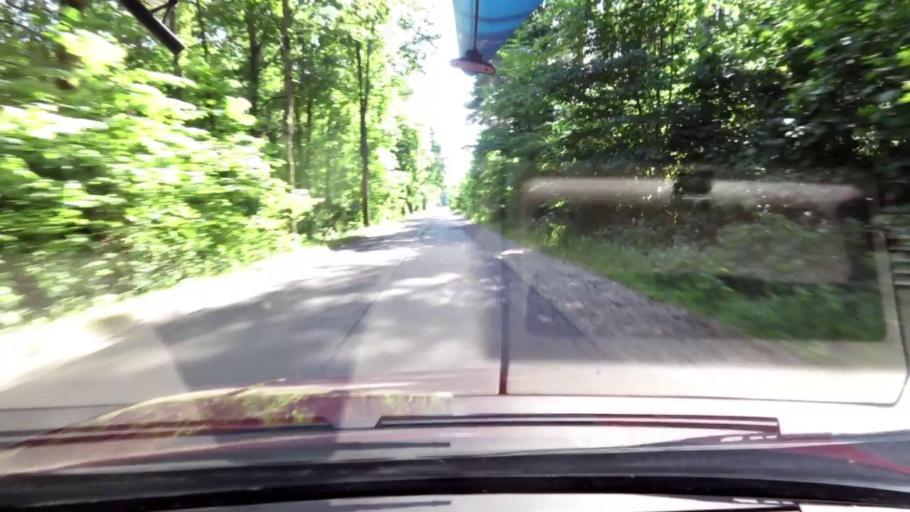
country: PL
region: Pomeranian Voivodeship
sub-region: Powiat slupski
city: Kobylnica
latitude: 54.3422
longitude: 16.9637
